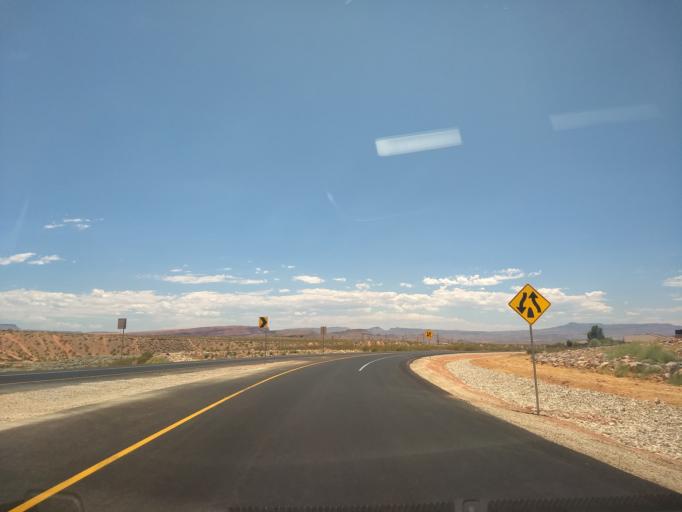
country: US
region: Utah
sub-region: Washington County
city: Washington
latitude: 37.1584
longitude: -113.5199
